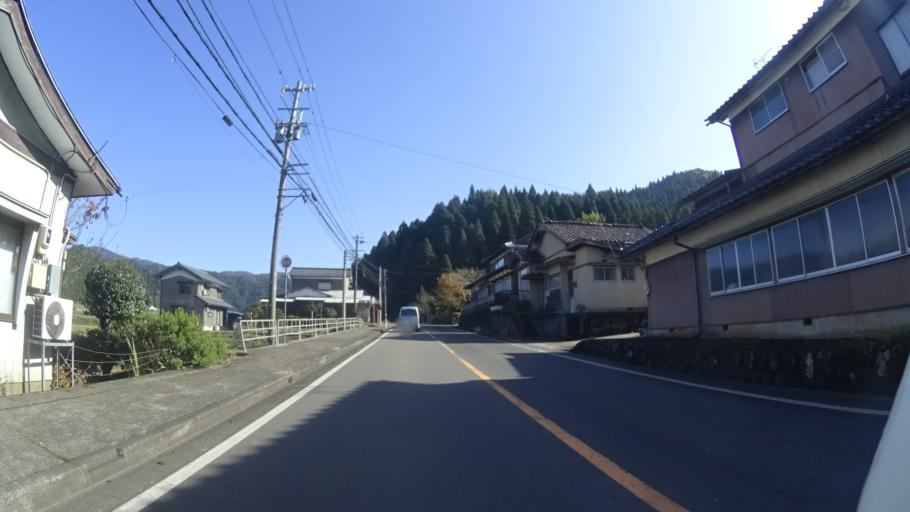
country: JP
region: Fukui
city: Sabae
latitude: 35.9358
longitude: 136.2918
